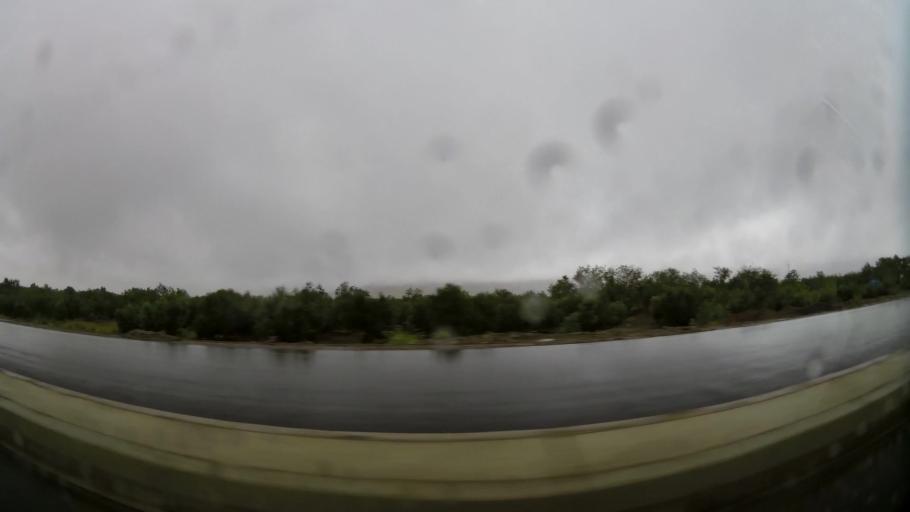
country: MA
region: Oriental
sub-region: Nador
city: Midar
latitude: 34.8523
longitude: -3.7219
